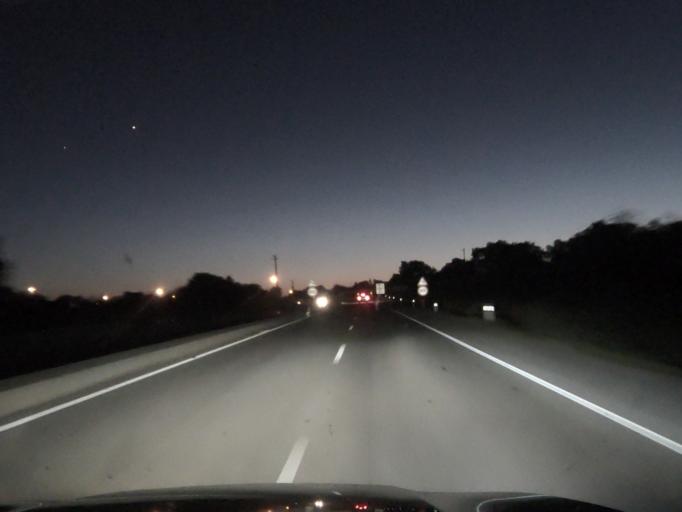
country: PT
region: Faro
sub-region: Loule
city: Loule
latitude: 37.1452
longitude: -8.0375
